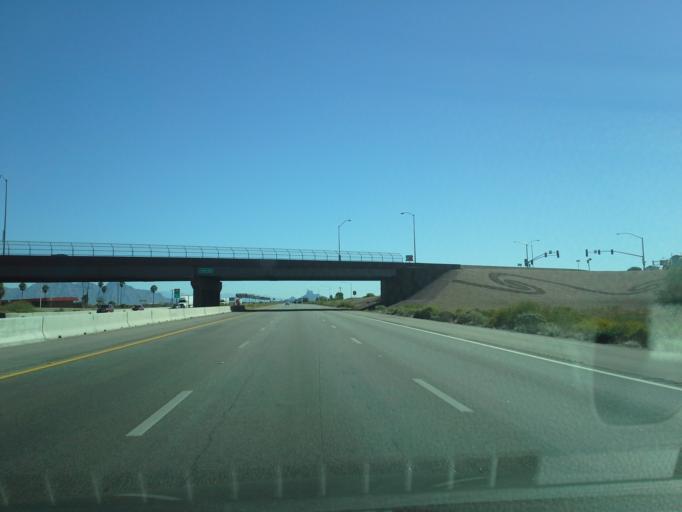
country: US
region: Arizona
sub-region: Pinal County
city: Arizona City
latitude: 32.7777
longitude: -111.6205
